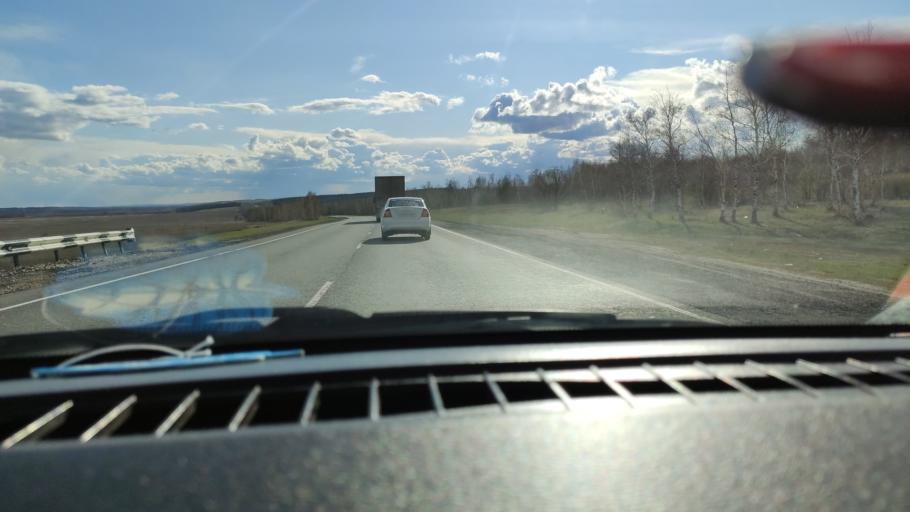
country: RU
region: Saratov
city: Sennoy
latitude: 52.1322
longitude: 46.8643
